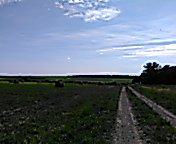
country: RU
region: Penza
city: Lermontovo
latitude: 52.9627
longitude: 43.6745
